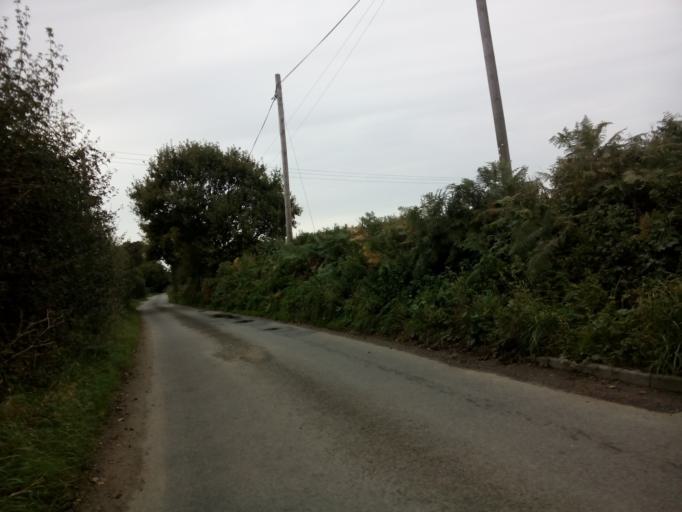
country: GB
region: England
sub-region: Suffolk
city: Ipswich
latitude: 52.0123
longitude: 1.1324
